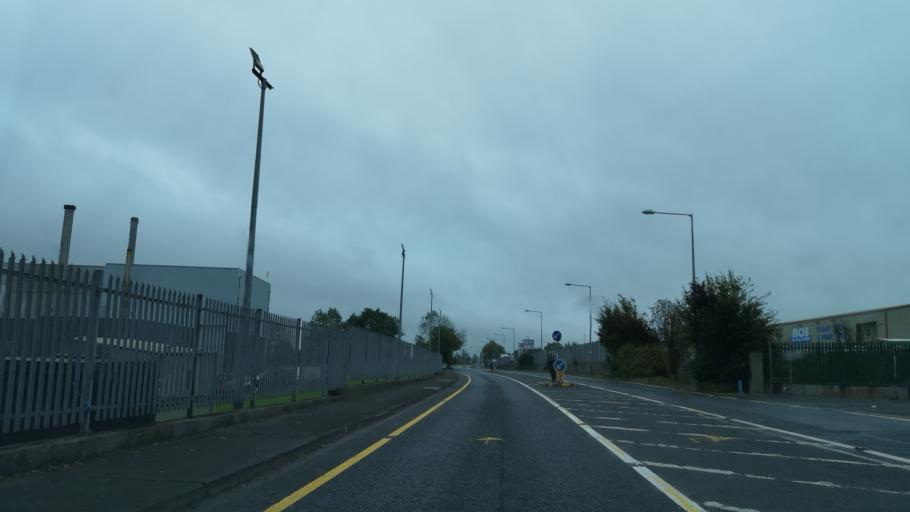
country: IE
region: Connaught
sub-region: Roscommon
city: Ballaghaderreen
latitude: 53.8975
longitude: -8.5695
